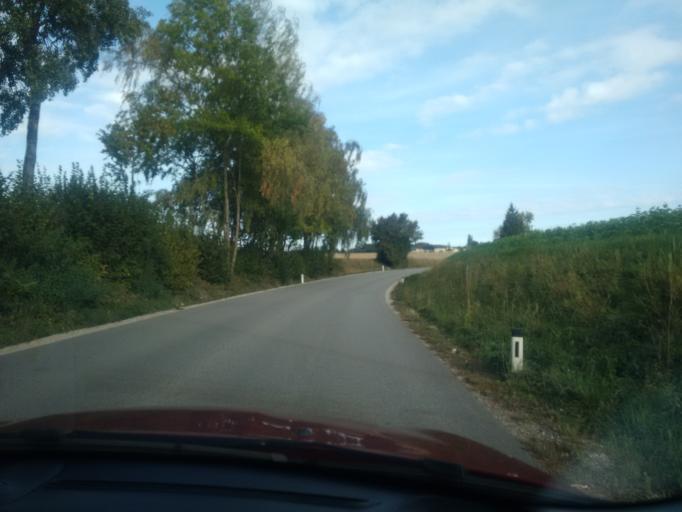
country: AT
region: Upper Austria
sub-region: Wels-Land
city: Steinhaus
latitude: 48.1243
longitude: 14.0248
